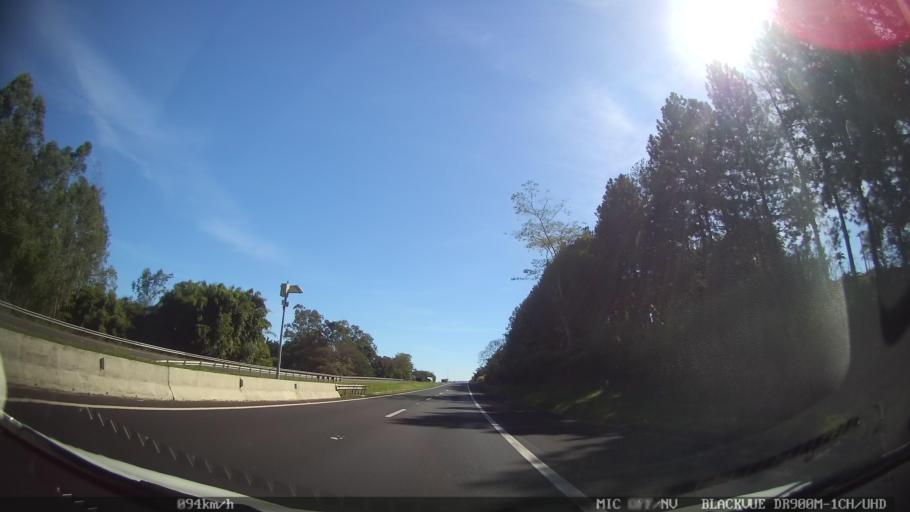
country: BR
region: Sao Paulo
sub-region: Santa Rita Do Passa Quatro
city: Santa Rita do Passa Quatro
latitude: -21.7512
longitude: -47.5698
